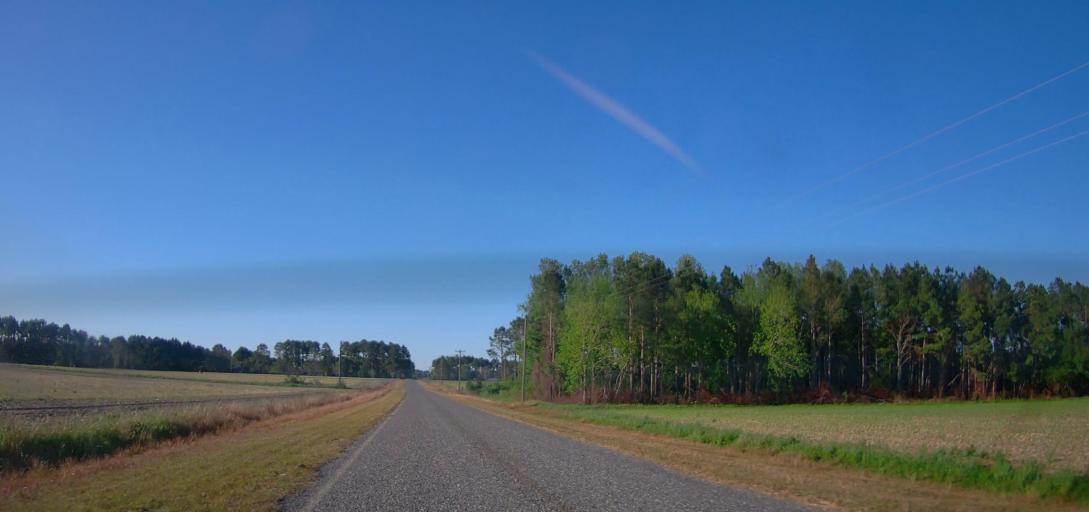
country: US
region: Georgia
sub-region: Ben Hill County
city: Fitzgerald
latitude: 31.6641
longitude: -83.1468
